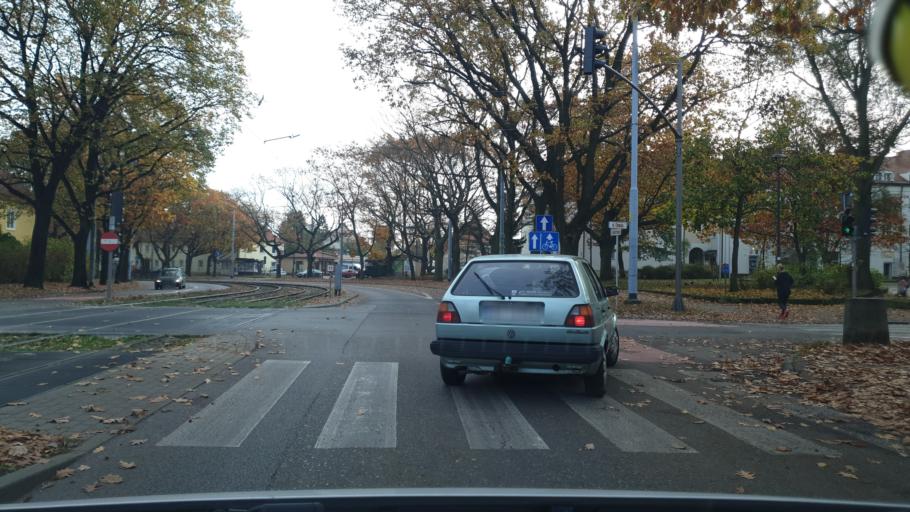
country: PL
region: Pomeranian Voivodeship
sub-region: Sopot
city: Sopot
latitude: 54.3874
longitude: 18.5831
